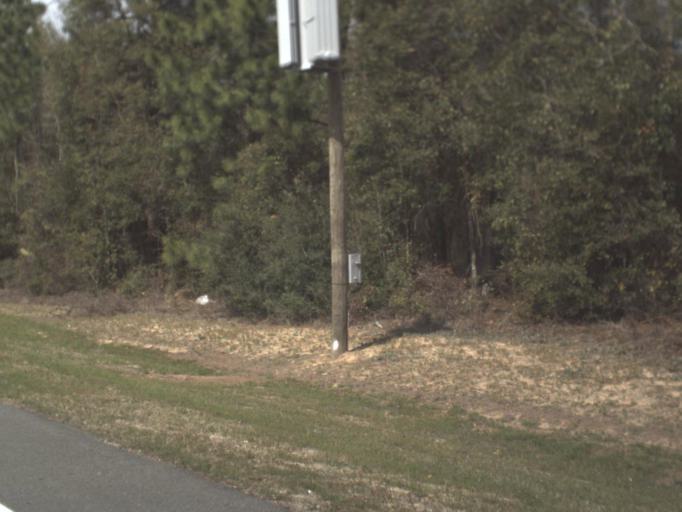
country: US
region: Florida
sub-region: Leon County
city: Tallahassee
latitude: 30.3979
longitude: -84.3407
